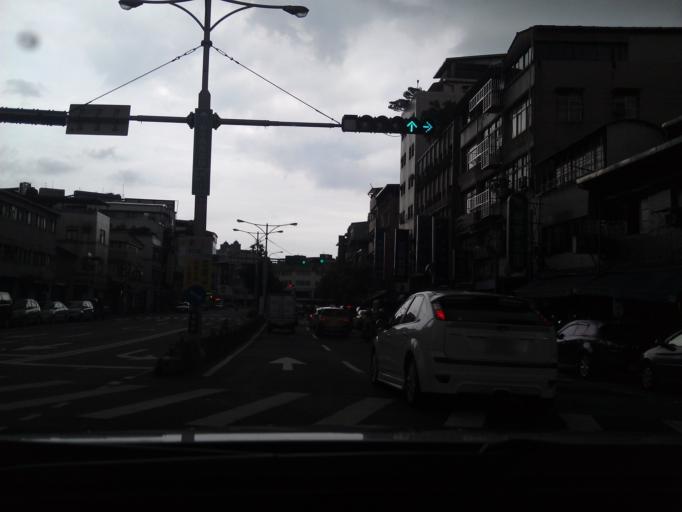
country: TW
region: Taipei
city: Taipei
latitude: 25.0340
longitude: 121.5047
